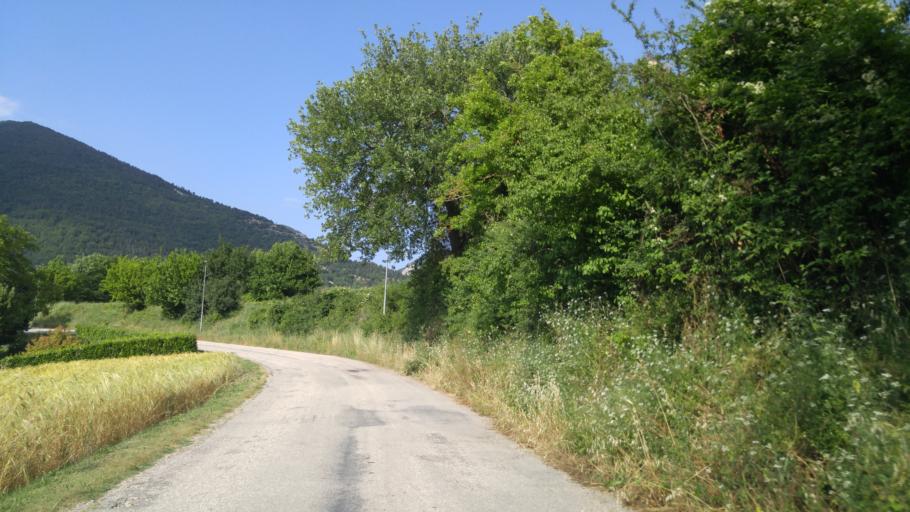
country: IT
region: The Marches
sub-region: Provincia di Pesaro e Urbino
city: Acqualagna
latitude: 43.6320
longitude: 12.6947
